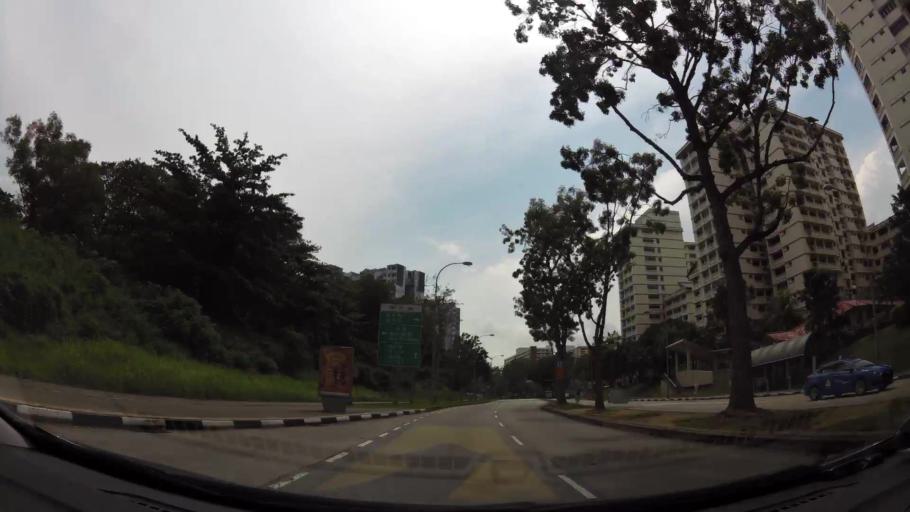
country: MY
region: Johor
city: Kampung Pasir Gudang Baru
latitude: 1.3825
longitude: 103.9386
